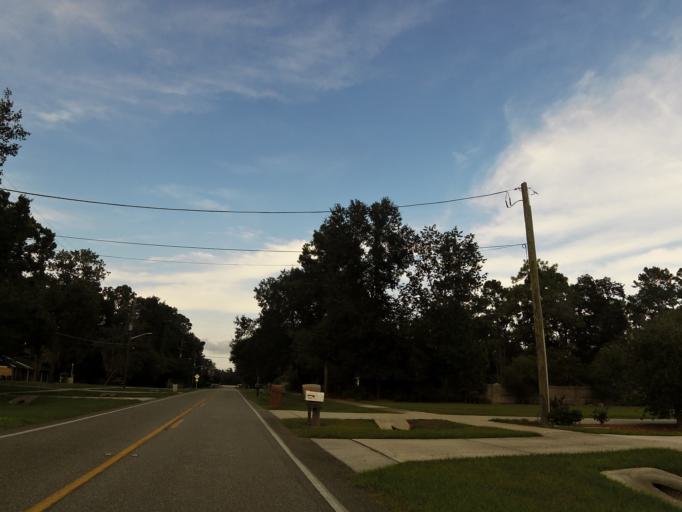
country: US
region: Florida
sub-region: Saint Johns County
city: Fruit Cove
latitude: 30.1023
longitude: -81.6308
